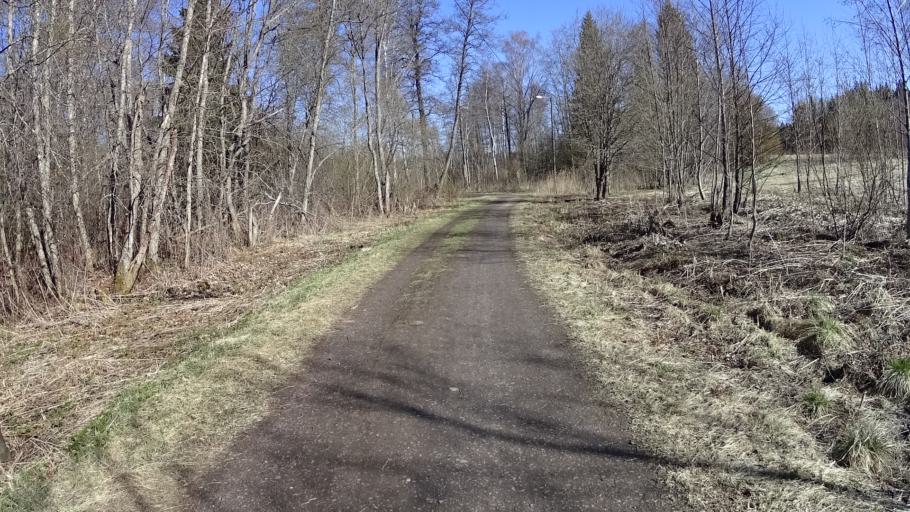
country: FI
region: Uusimaa
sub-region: Helsinki
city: Espoo
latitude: 60.2258
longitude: 24.6614
